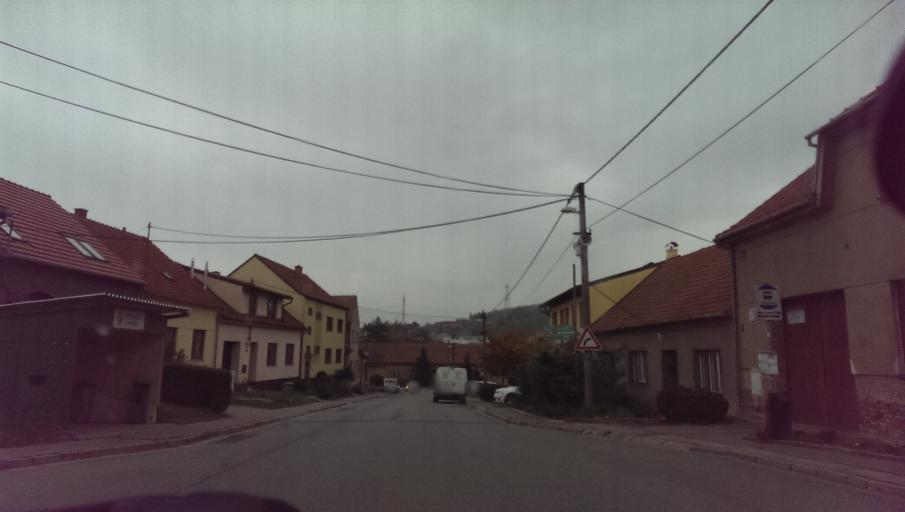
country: CZ
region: South Moravian
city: Ostopovice
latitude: 49.1418
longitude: 16.5538
